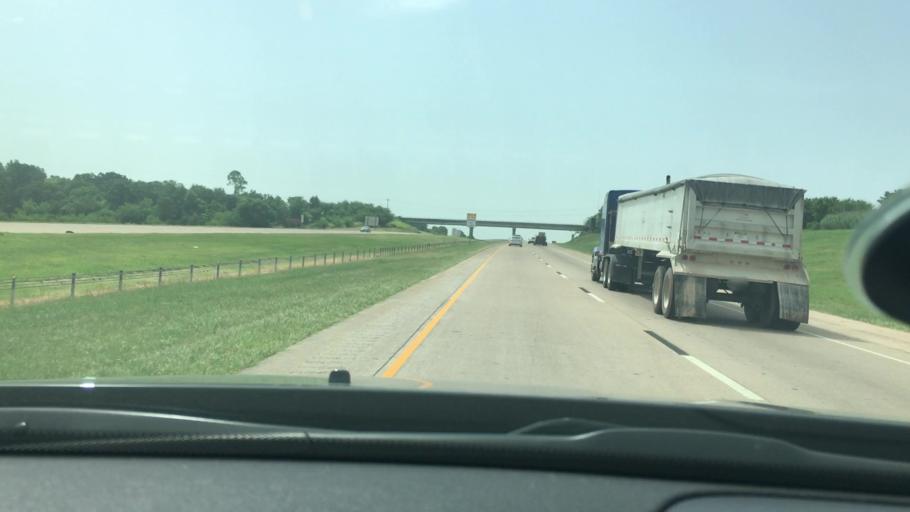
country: US
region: Oklahoma
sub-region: Garvin County
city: Pauls Valley
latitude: 34.7277
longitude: -97.2555
